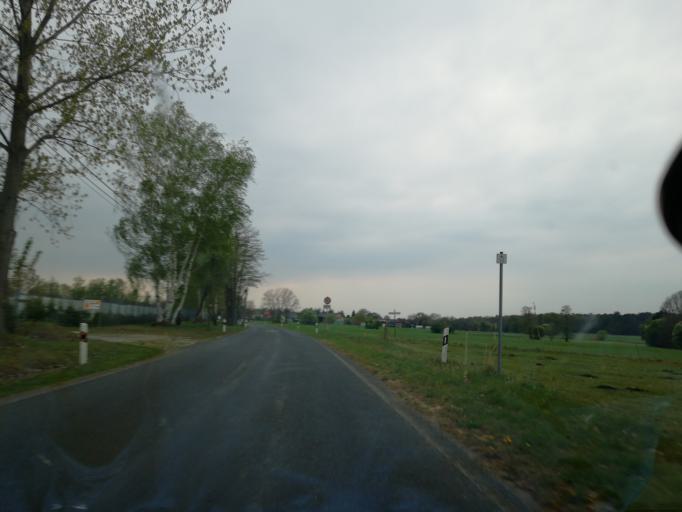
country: DE
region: Brandenburg
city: Lubbenau
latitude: 51.8212
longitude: 13.9090
